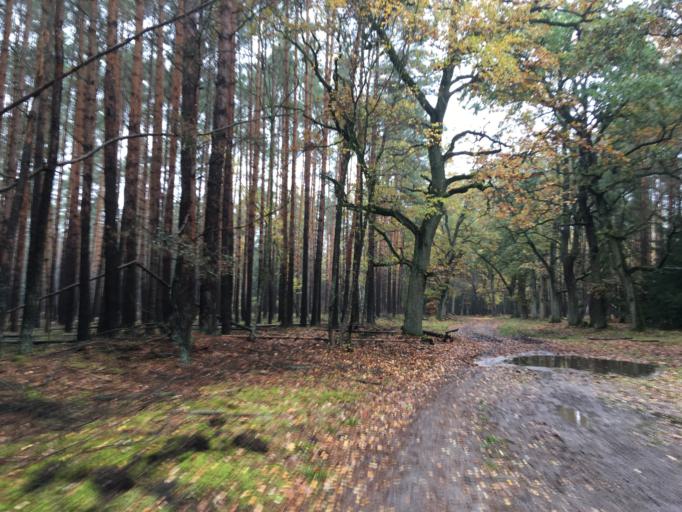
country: DE
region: Brandenburg
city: Beeskow
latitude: 52.2198
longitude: 14.3007
